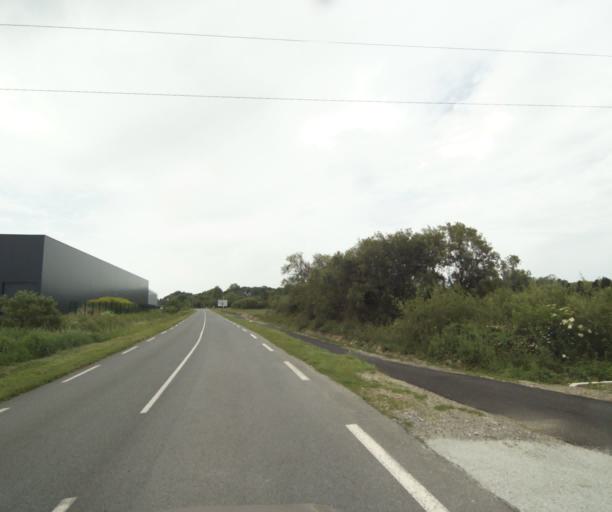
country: FR
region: Aquitaine
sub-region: Departement des Pyrenees-Atlantiques
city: Mouguerre
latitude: 43.4917
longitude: -1.4206
